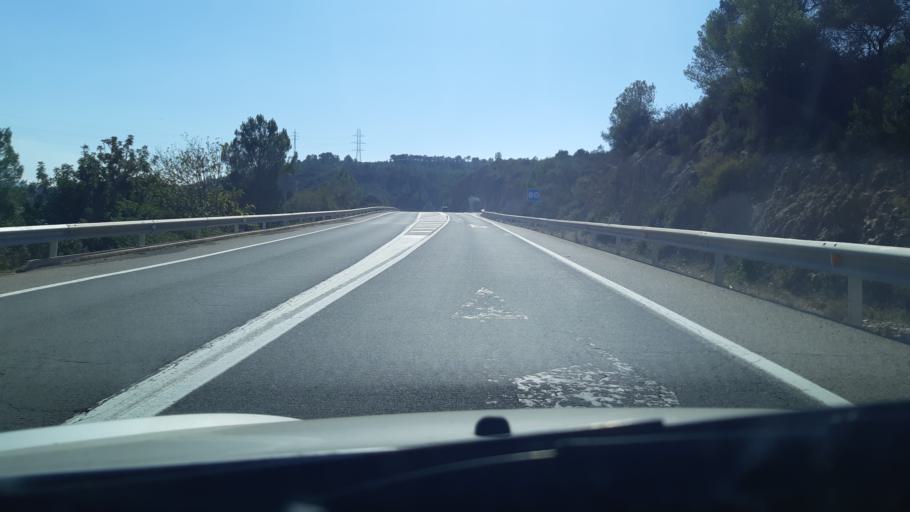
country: ES
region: Catalonia
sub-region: Provincia de Tarragona
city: Tivenys
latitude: 40.9338
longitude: 0.4851
